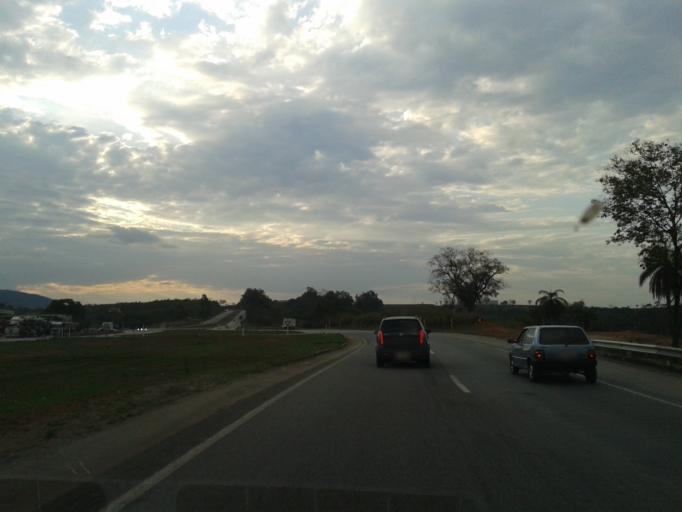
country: BR
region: Minas Gerais
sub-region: Juatuba
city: Juatuba
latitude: -19.9572
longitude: -44.3631
